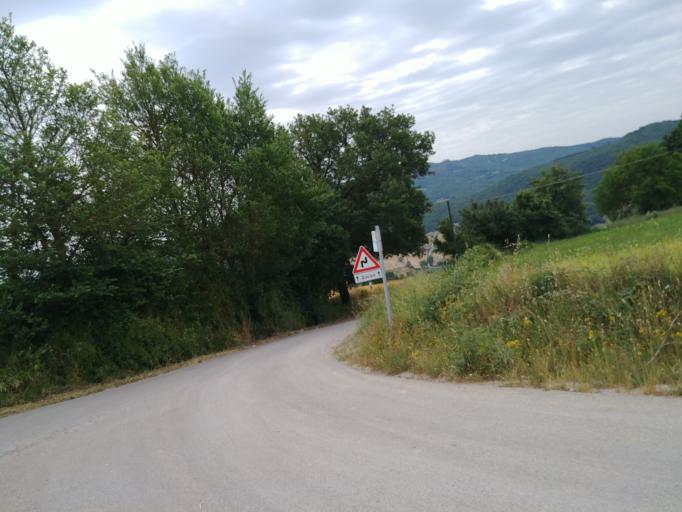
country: IT
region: Umbria
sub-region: Provincia di Perugia
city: Pistrino
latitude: 43.4821
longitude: 12.1647
